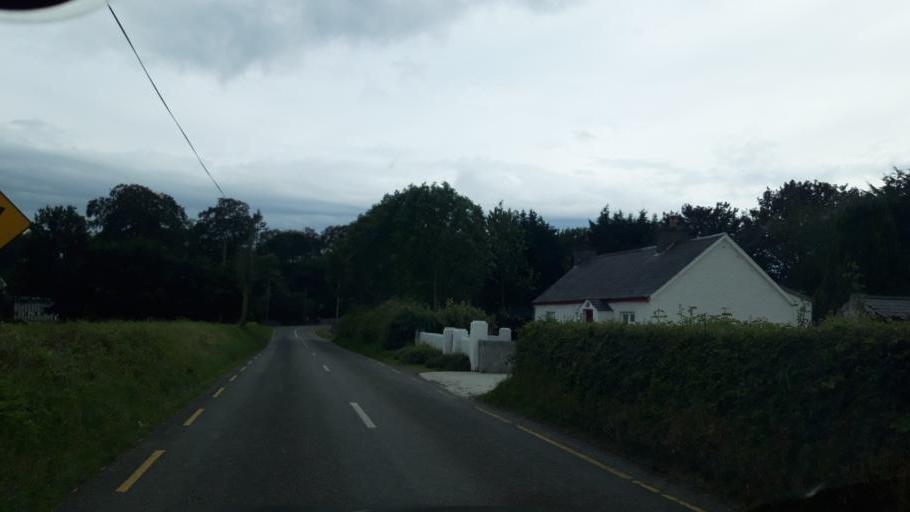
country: IE
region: Leinster
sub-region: Kilkenny
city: Ballyragget
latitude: 52.7686
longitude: -7.3539
